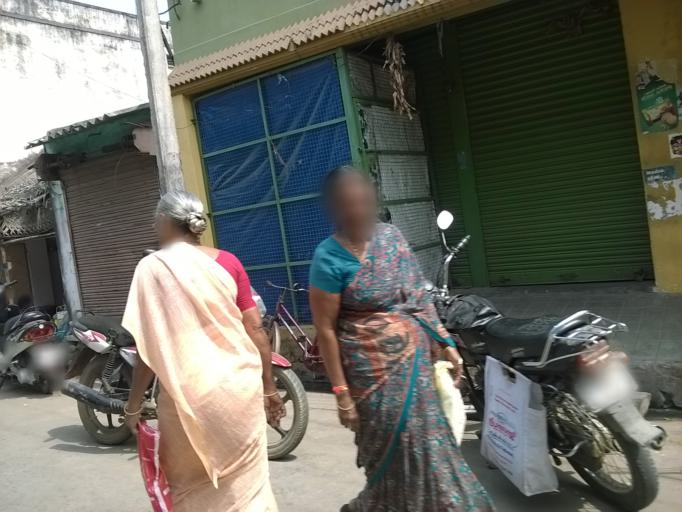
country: IN
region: Tamil Nadu
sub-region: Cuddalore
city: Panruti
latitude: 11.7743
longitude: 79.5491
